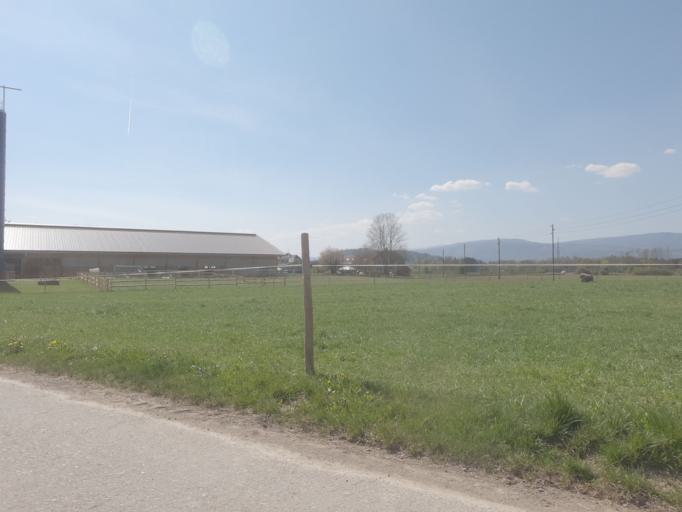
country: CH
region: Bern
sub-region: Biel/Bienne District
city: Orpund
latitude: 47.1109
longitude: 7.3349
